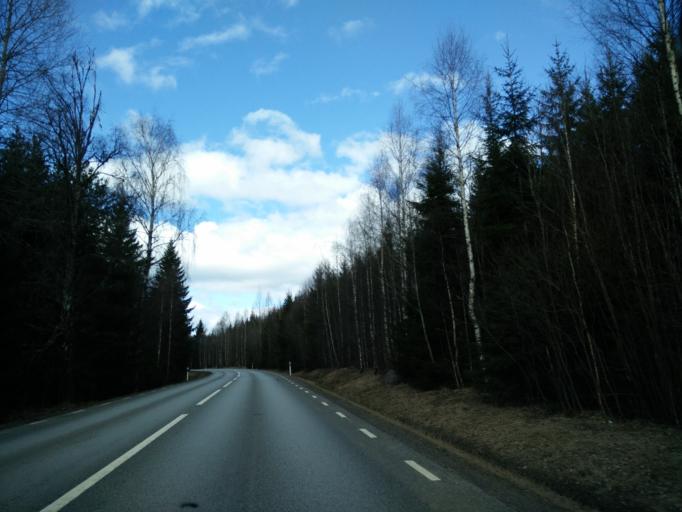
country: SE
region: Vaermland
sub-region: Munkfors Kommun
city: Munkfors
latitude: 59.9475
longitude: 13.5807
